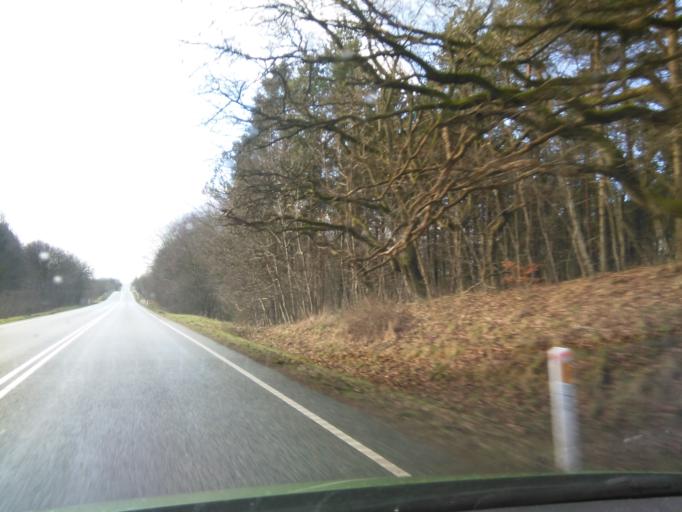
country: DK
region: Central Jutland
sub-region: Skanderborg Kommune
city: Skanderborg
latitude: 56.0252
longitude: 9.9027
